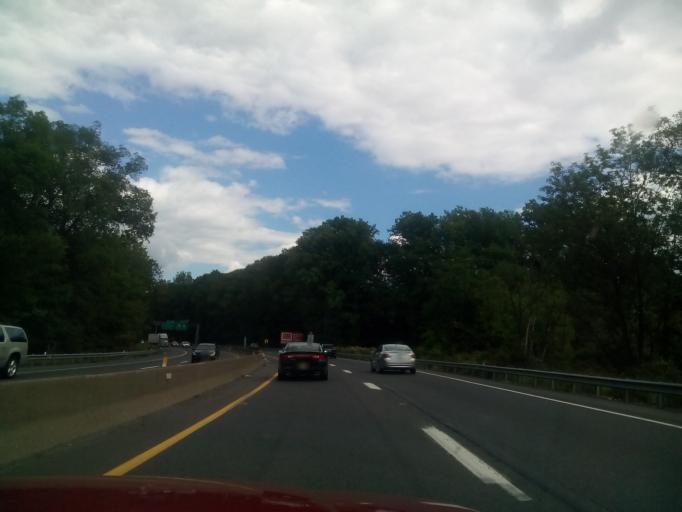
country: US
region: Pennsylvania
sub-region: Monroe County
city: Stroudsburg
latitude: 40.9787
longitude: -75.1977
